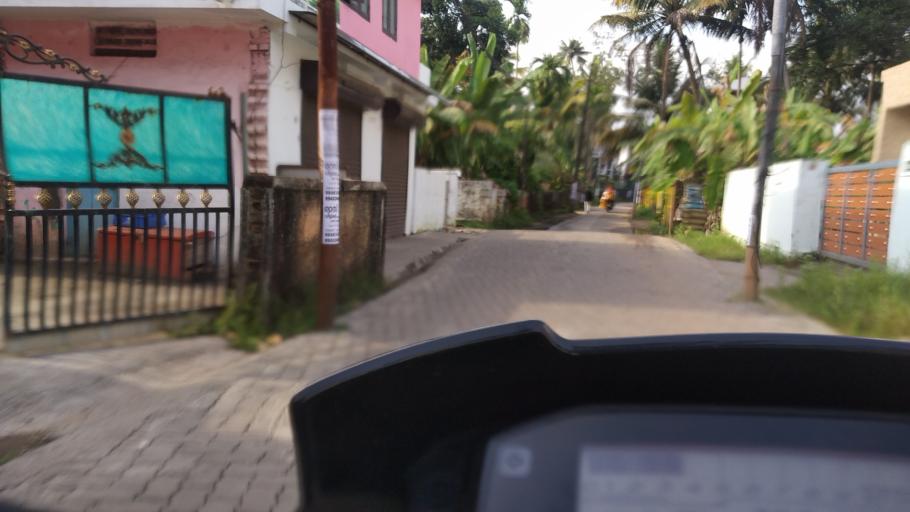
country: IN
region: Kerala
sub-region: Ernakulam
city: Cochin
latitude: 9.9936
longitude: 76.2648
